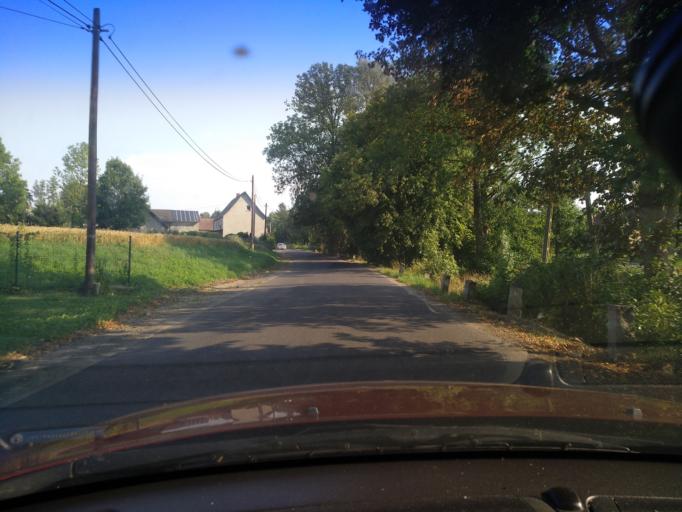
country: PL
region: Lower Silesian Voivodeship
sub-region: Powiat lubanski
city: Siekierczyn
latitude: 51.0810
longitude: 15.1500
